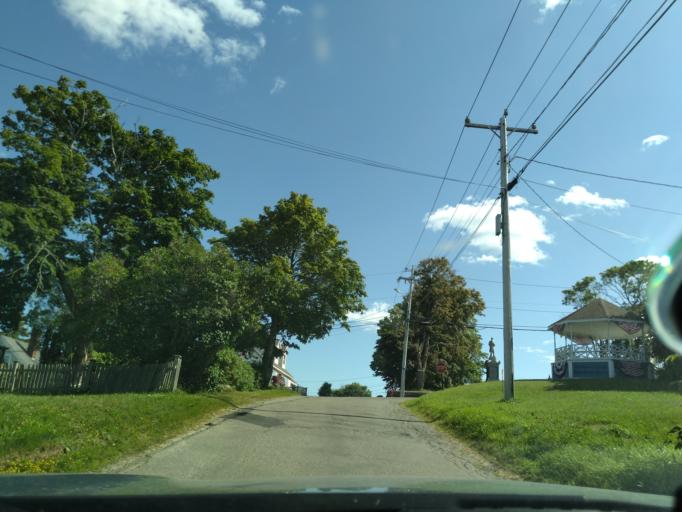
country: US
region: Maine
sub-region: Washington County
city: Eastport
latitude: 44.8619
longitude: -66.9845
